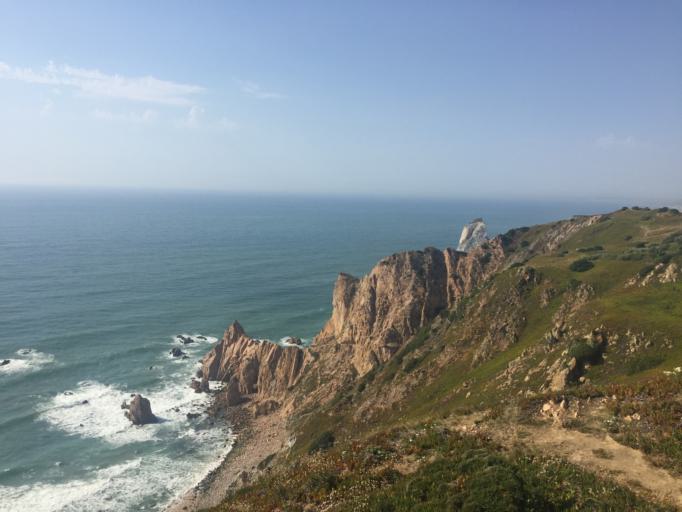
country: PT
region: Lisbon
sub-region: Sintra
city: Colares
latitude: 38.7842
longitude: -9.4949
